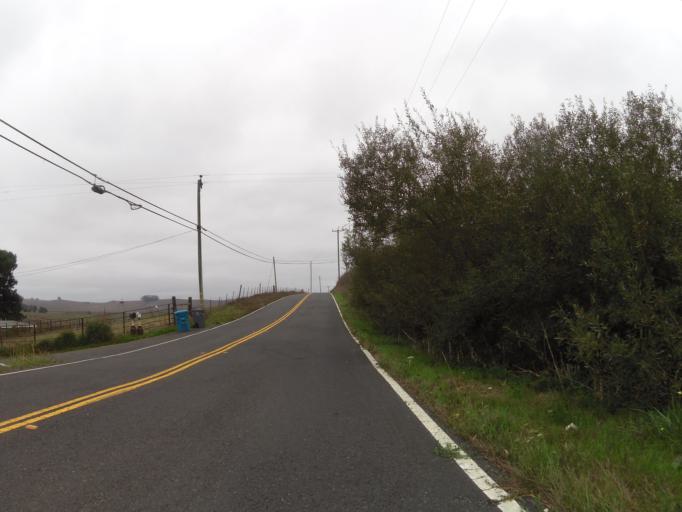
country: US
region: California
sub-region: Sonoma County
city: Occidental
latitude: 38.2875
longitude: -122.8991
